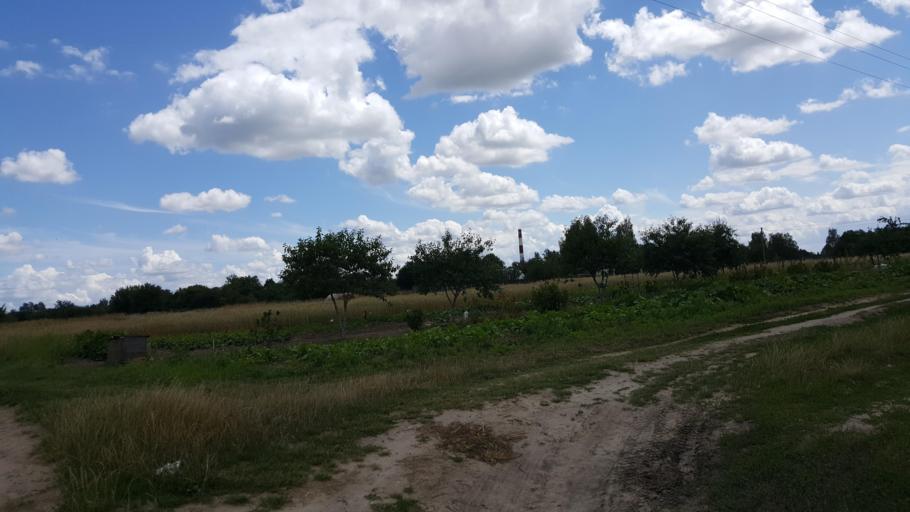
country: BY
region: Brest
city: Kamyanyets
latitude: 52.3225
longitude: 23.9295
